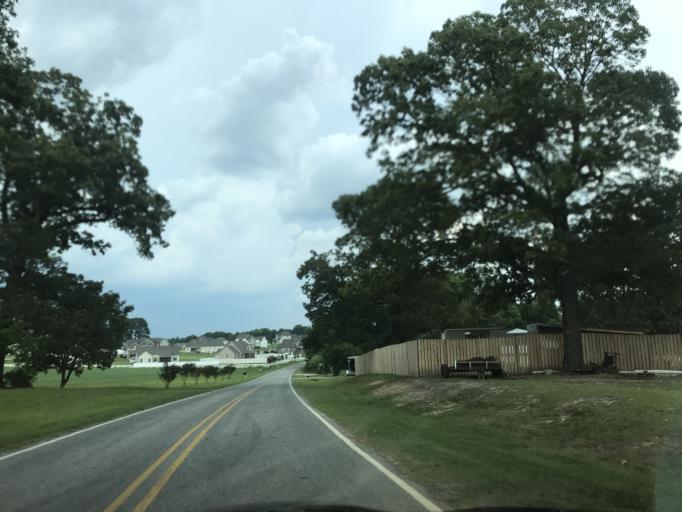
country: US
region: North Carolina
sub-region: Johnston County
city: Four Oaks
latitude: 35.5142
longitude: -78.5358
